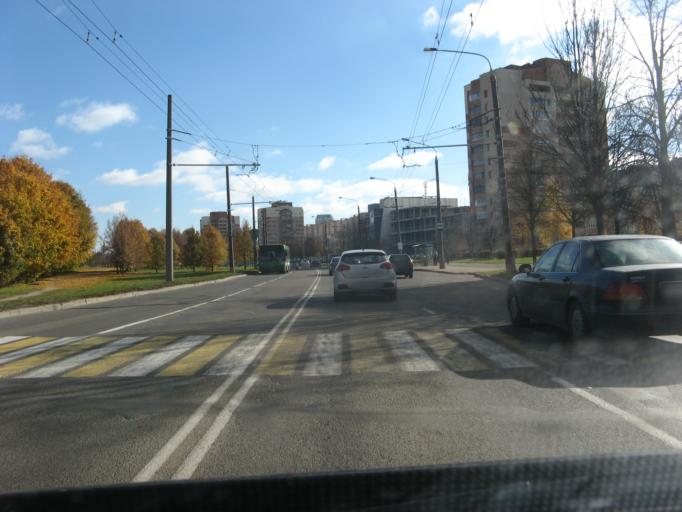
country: BY
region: Minsk
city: Novoye Medvezhino
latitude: 53.8726
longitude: 27.4696
